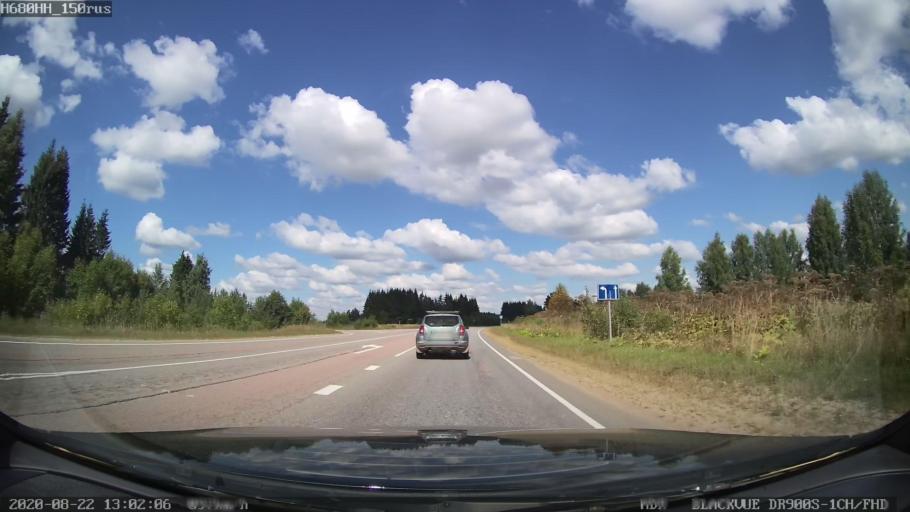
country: RU
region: Tverskaya
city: Bezhetsk
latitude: 57.6448
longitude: 36.3947
